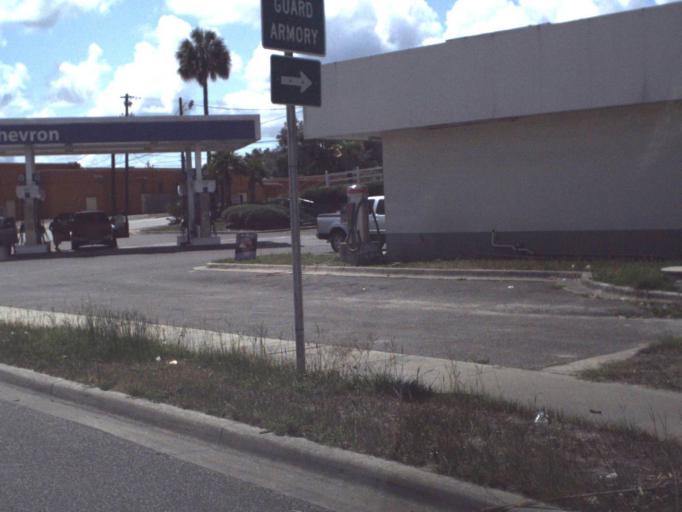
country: US
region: Florida
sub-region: Putnam County
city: Palatka
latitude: 29.6504
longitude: -81.6504
